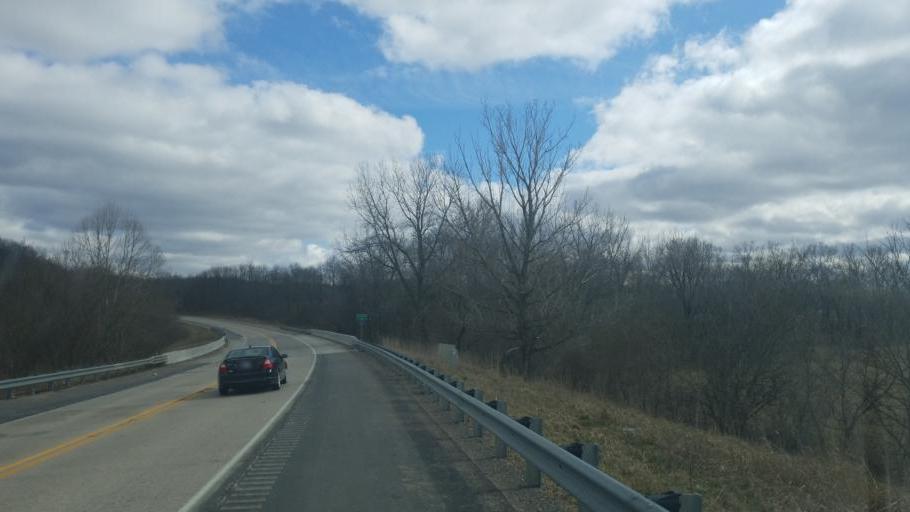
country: US
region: Indiana
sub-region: Parke County
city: Montezuma
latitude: 39.7763
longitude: -87.3307
